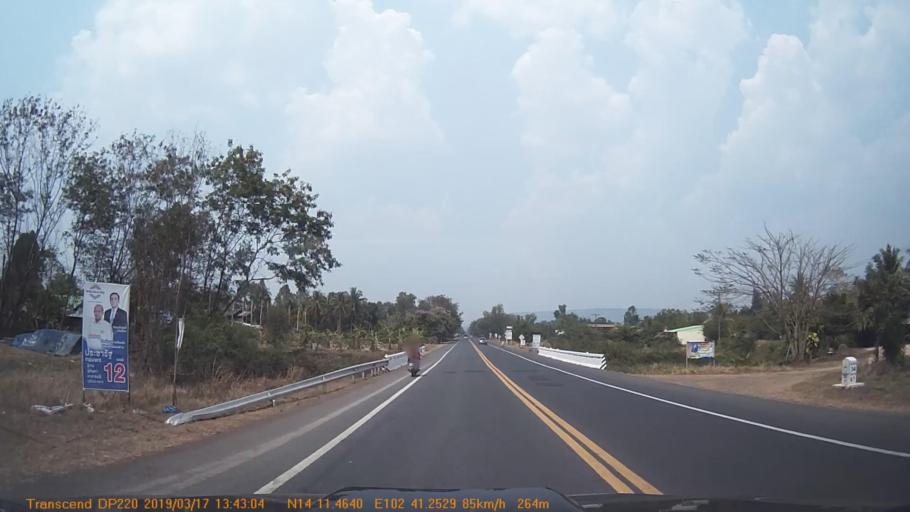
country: TH
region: Buriram
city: Non Din Daeng
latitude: 14.1913
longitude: 102.6877
